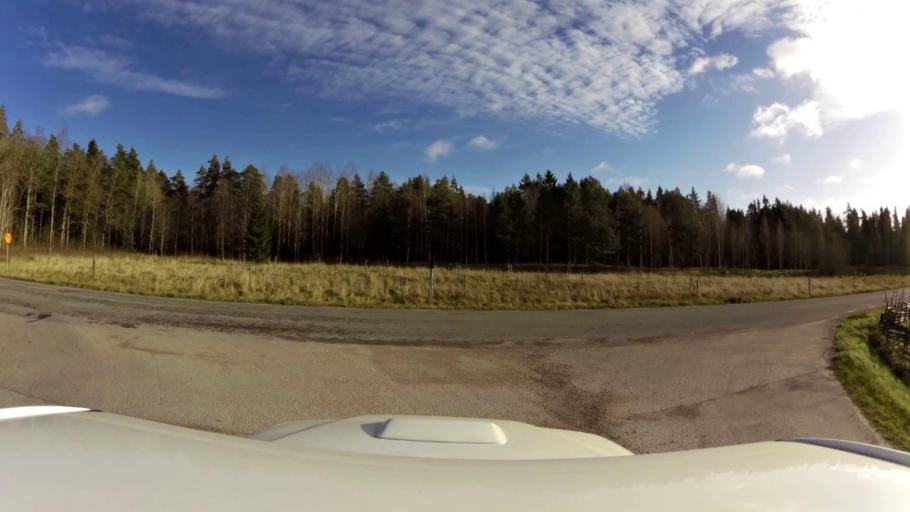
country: SE
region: OEstergoetland
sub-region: Linkopings Kommun
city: Linkoping
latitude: 58.3715
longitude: 15.6267
